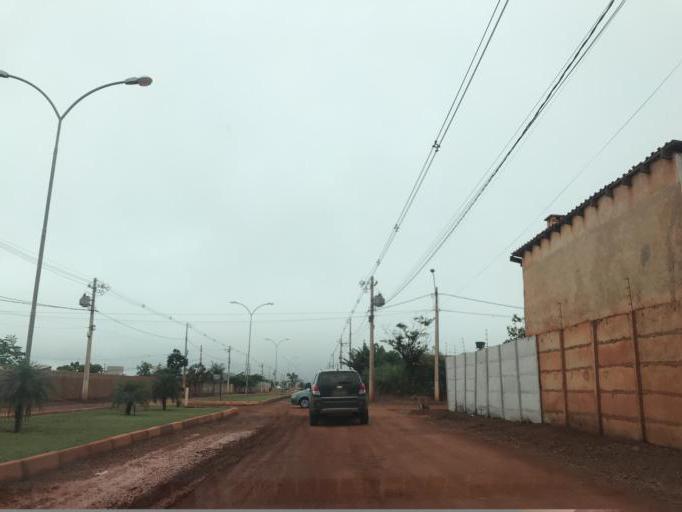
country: BR
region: Federal District
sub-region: Brasilia
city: Brasilia
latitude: -15.8269
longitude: -47.7942
